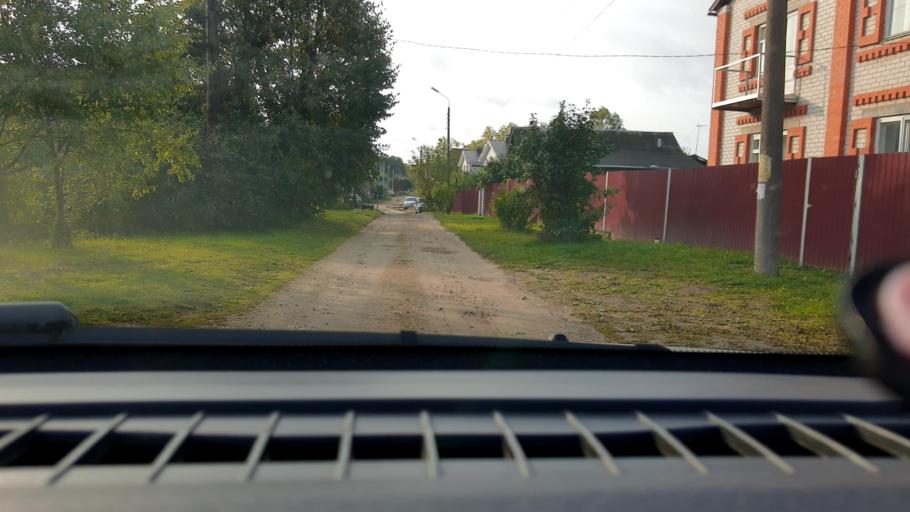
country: RU
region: Nizjnij Novgorod
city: Kstovo
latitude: 56.1888
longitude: 44.1602
